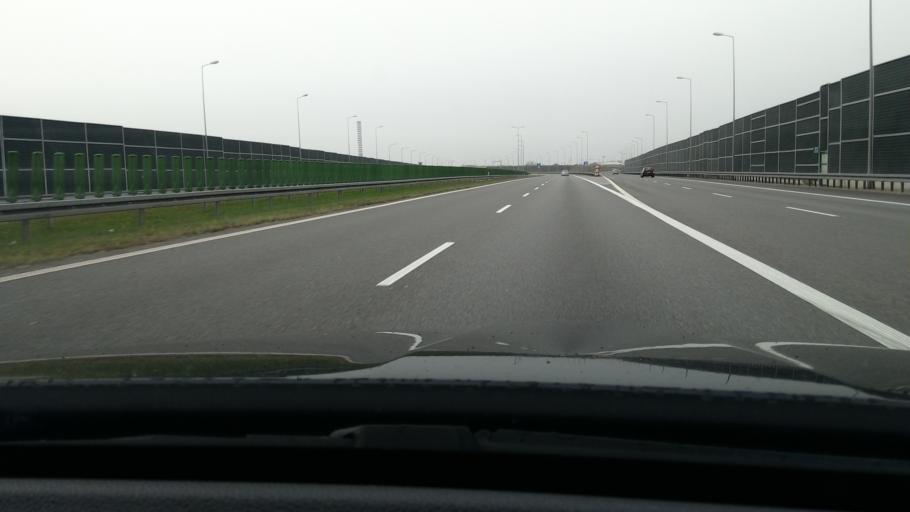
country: PL
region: Masovian Voivodeship
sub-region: Powiat warszawski zachodni
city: Ozarow Mazowiecki
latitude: 52.1897
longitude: 20.7884
